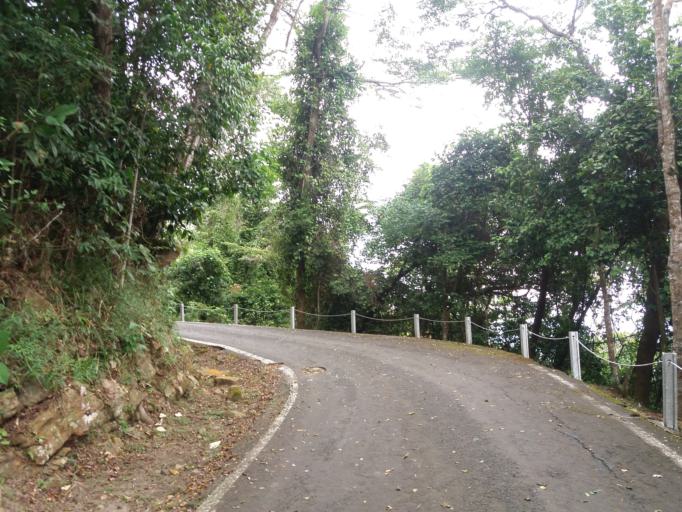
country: PA
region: Panama
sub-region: Distrito de Panama
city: Ancon
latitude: 8.9588
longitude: -79.5485
